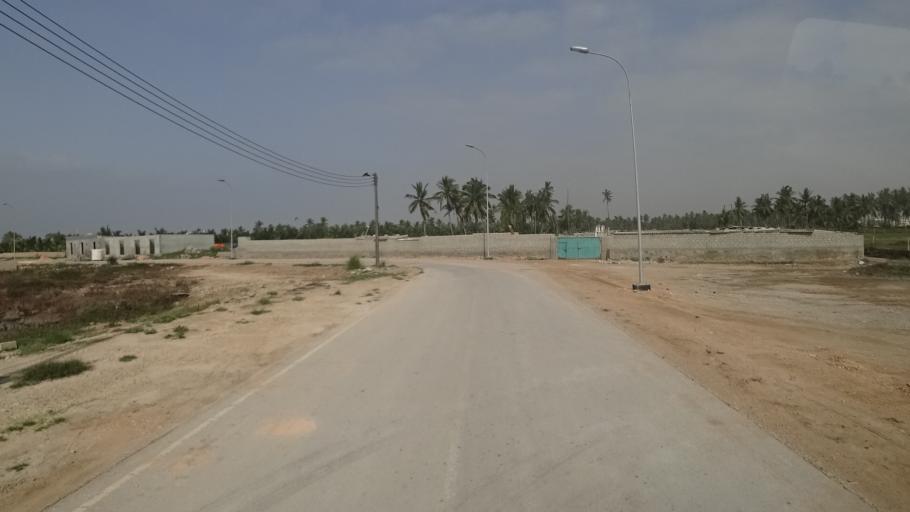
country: OM
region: Zufar
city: Salalah
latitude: 17.0159
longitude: 54.1710
